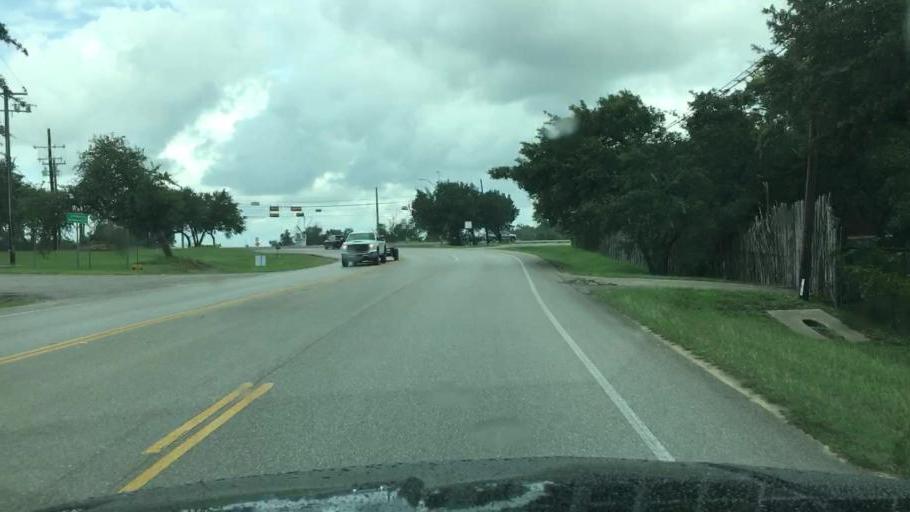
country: US
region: Texas
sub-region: Travis County
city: Bee Cave
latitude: 30.2074
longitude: -97.9731
